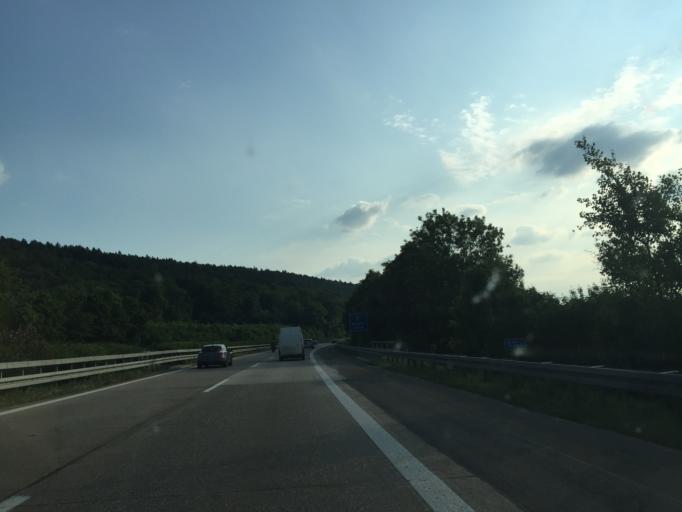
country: DE
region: Baden-Wuerttemberg
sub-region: Regierungsbezirk Stuttgart
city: Eberstadt
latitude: 49.1745
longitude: 9.3343
